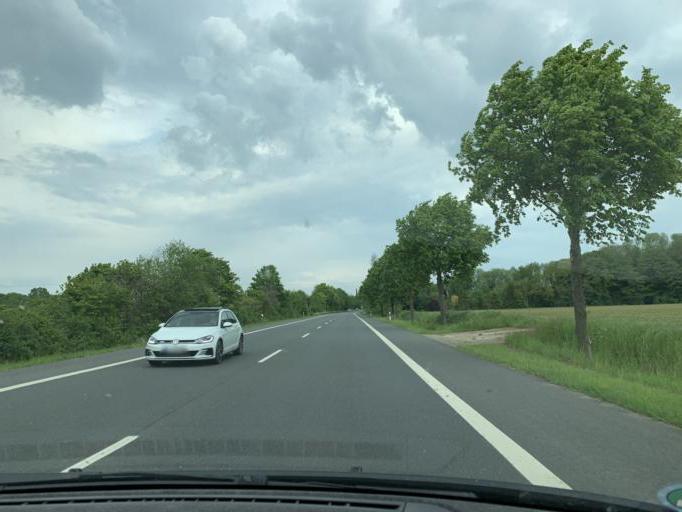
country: DE
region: North Rhine-Westphalia
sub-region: Regierungsbezirk Koln
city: Vettweiss
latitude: 50.7568
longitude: 6.6378
